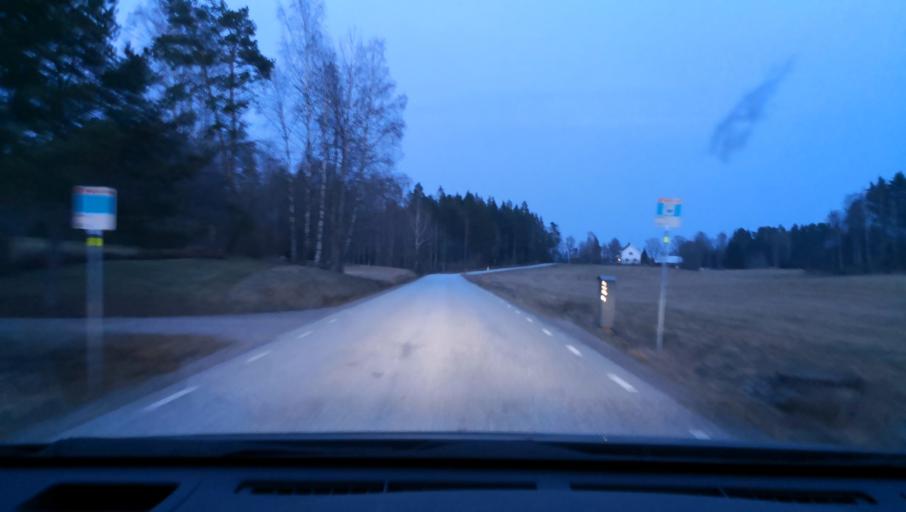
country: SE
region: OErebro
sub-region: Lindesbergs Kommun
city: Frovi
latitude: 59.5846
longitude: 15.4502
